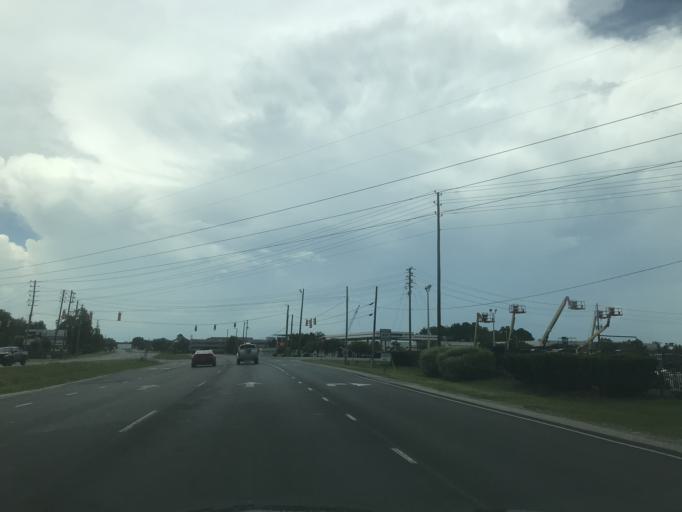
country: US
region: North Carolina
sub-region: Johnston County
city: Clayton
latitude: 35.6128
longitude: -78.4175
